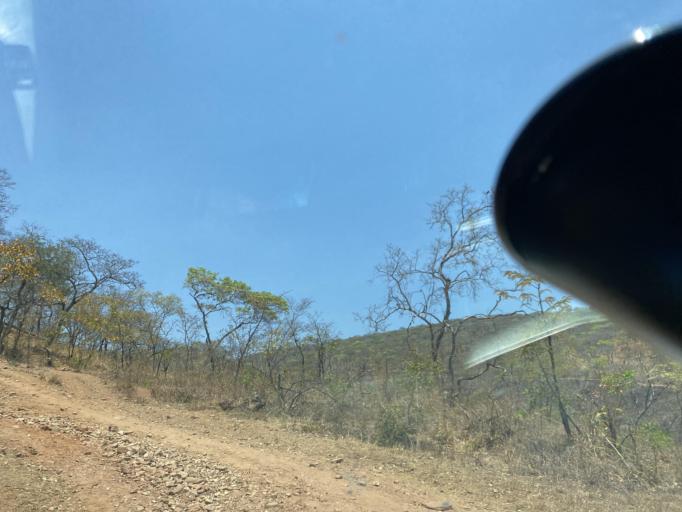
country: ZM
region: Lusaka
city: Kafue
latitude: -15.8081
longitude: 28.4365
